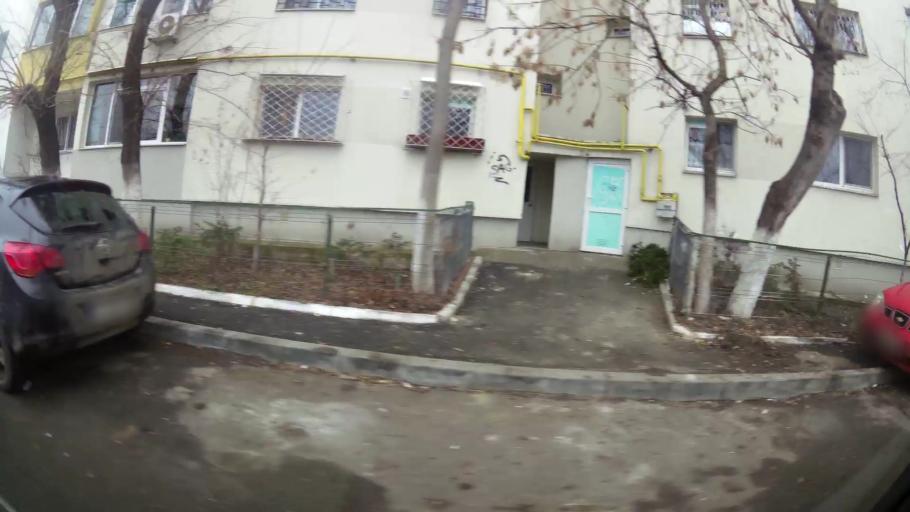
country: RO
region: Ilfov
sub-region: Comuna Popesti-Leordeni
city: Popesti-Leordeni
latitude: 44.4128
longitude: 26.1538
